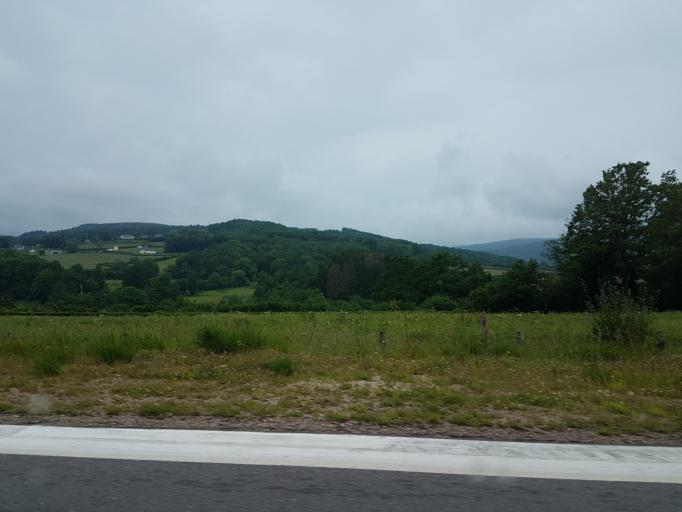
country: FR
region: Bourgogne
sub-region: Departement de la Nievre
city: Chateau-Chinon(Ville)
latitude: 47.0510
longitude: 3.9757
